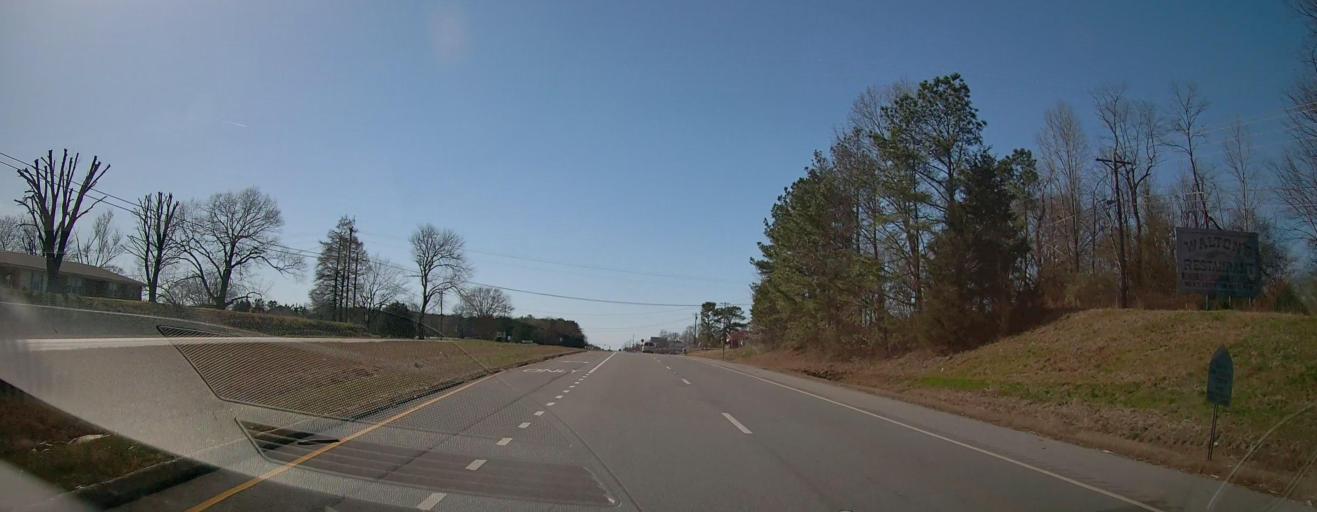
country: US
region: Alabama
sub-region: Lauderdale County
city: Rogersville
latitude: 34.8463
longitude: -87.3809
